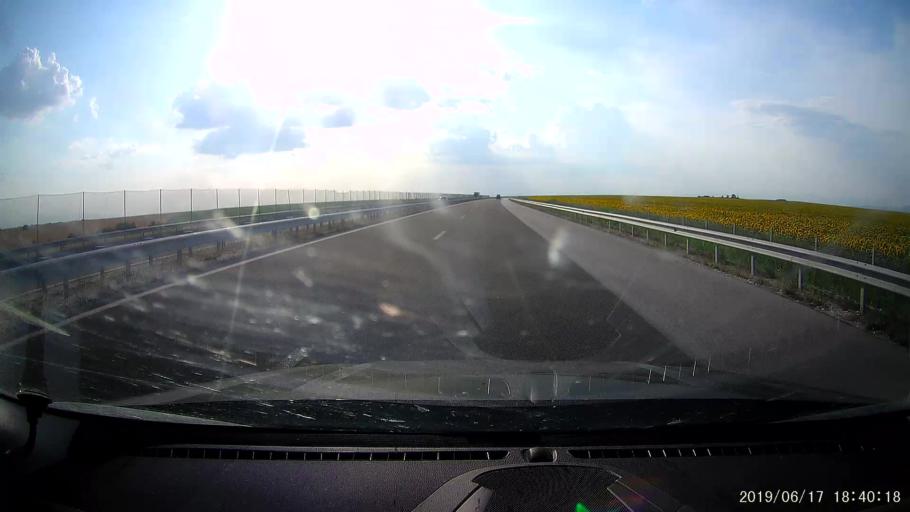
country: BG
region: Stara Zagora
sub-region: Obshtina Chirpan
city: Chirpan
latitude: 42.1538
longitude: 25.2816
